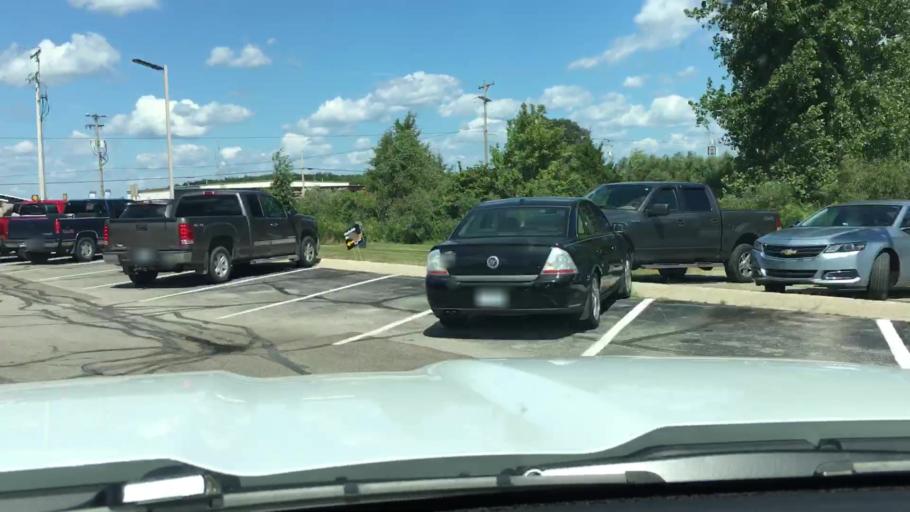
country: US
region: Michigan
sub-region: Saginaw County
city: Chesaning
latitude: 43.1859
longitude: -84.1672
